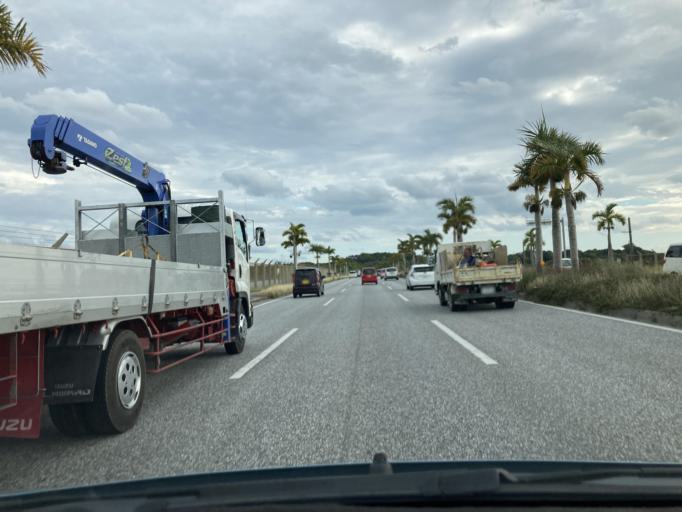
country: JP
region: Okinawa
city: Chatan
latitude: 26.3421
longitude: 127.7494
